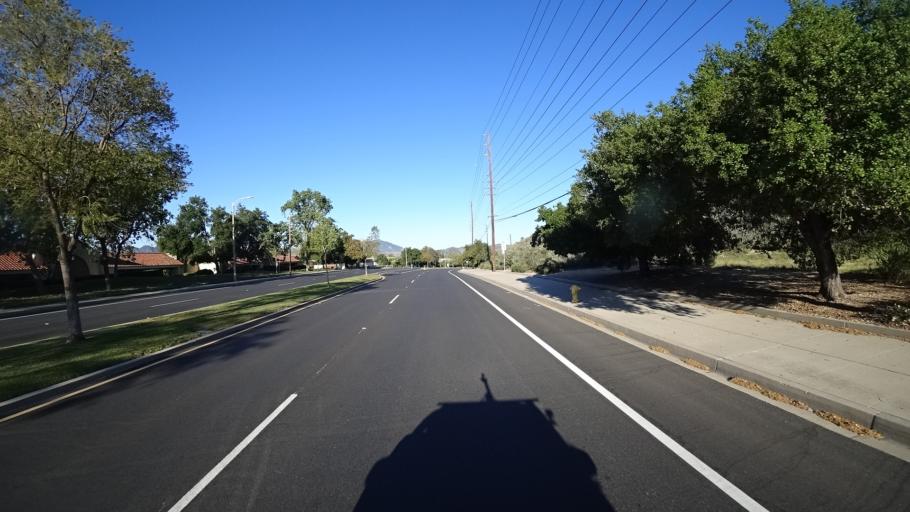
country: US
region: California
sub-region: Los Angeles County
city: Westlake Village
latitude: 34.1568
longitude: -118.8090
